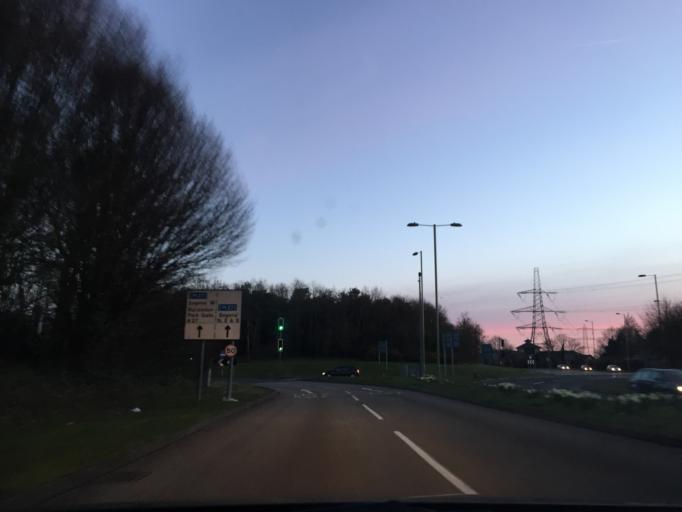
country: GB
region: England
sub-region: Hampshire
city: Botley
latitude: 50.8676
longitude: -1.2554
